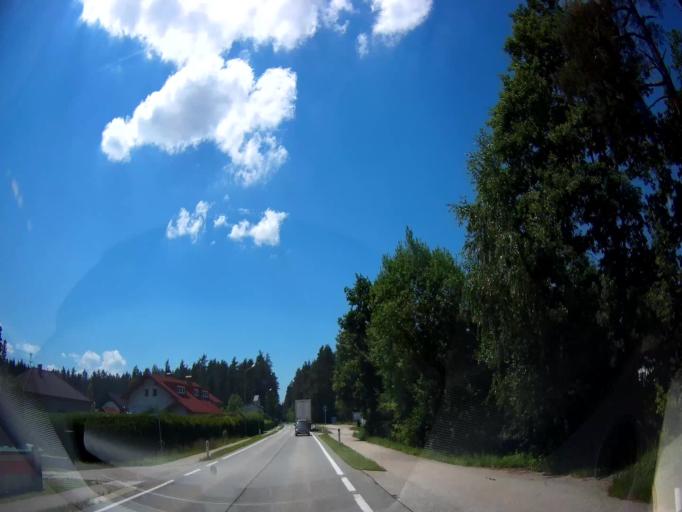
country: AT
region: Carinthia
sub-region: Politischer Bezirk Volkermarkt
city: Globasnitz
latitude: 46.6073
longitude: 14.7034
